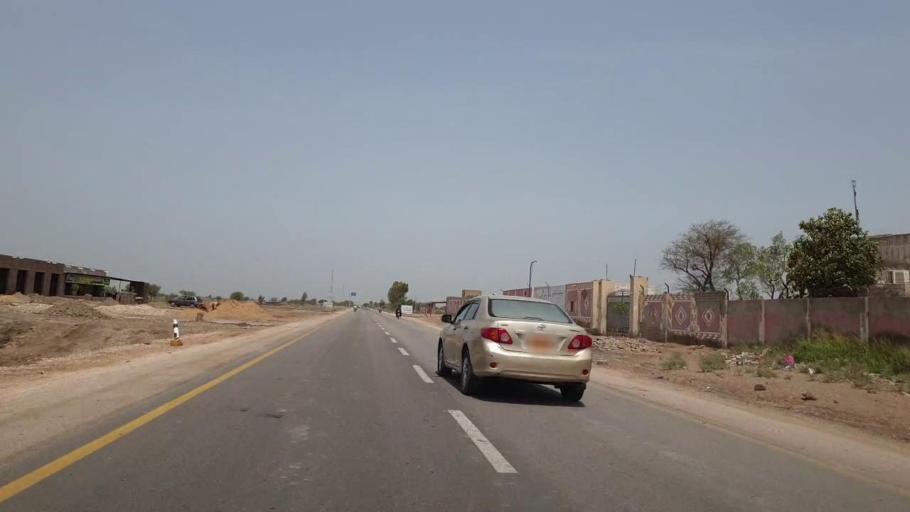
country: PK
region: Sindh
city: Shahpur Chakar
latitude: 26.1953
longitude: 68.5672
